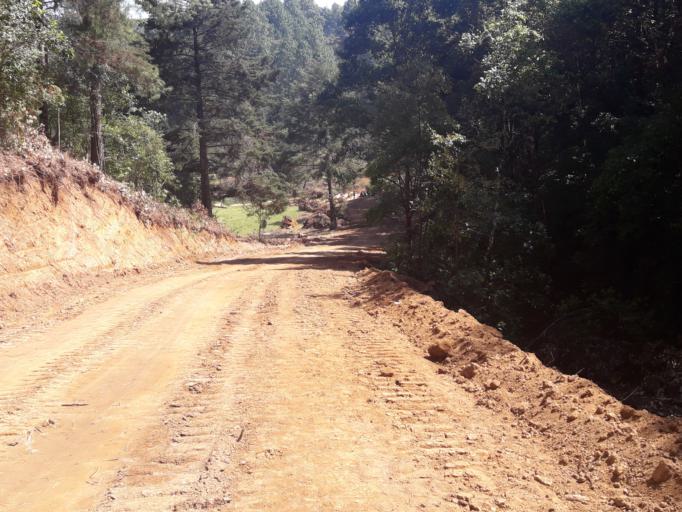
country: GT
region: Quiche
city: Nebaj
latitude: 15.4268
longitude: -91.1364
